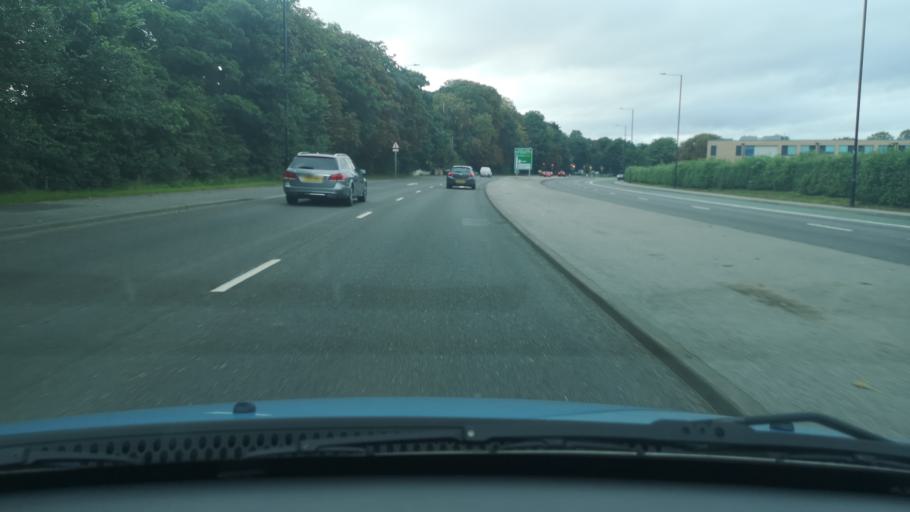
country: GB
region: England
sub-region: Doncaster
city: Bentley
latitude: 53.5447
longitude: -1.1741
